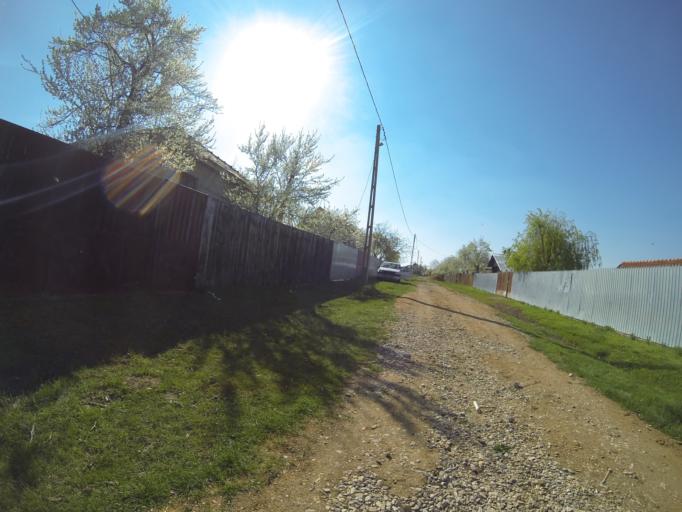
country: RO
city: Varvoru
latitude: 44.2265
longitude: 23.6548
